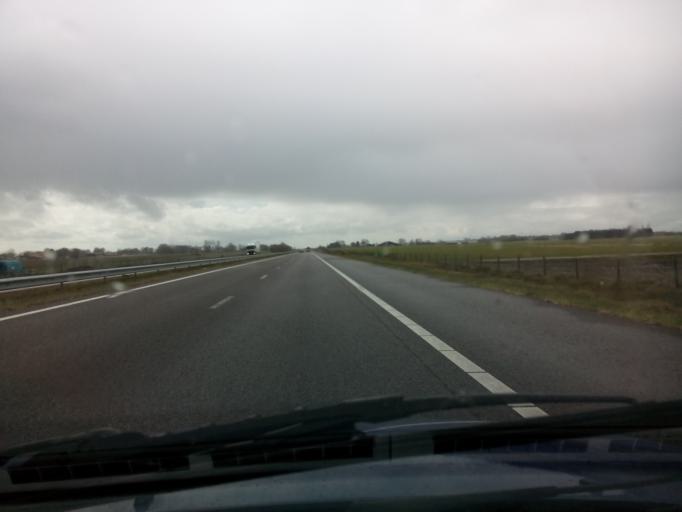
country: NL
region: Drenthe
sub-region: Gemeente Emmen
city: Klazienaveen
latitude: 52.7293
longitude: 6.9422
